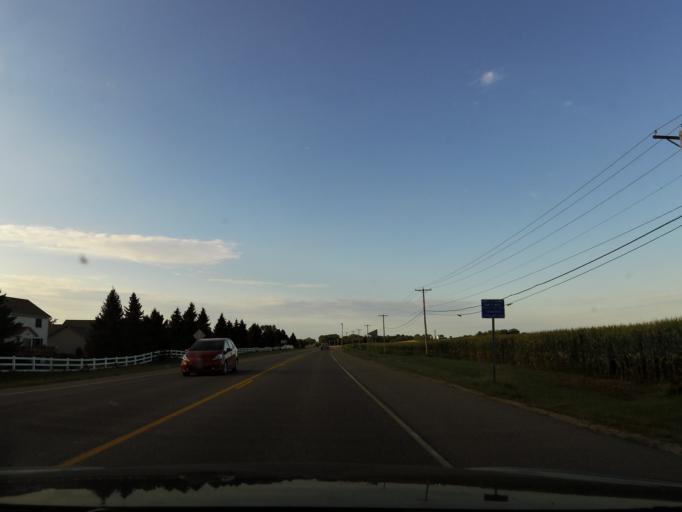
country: US
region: Minnesota
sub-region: Washington County
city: Cottage Grove
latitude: 44.8349
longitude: -92.9037
